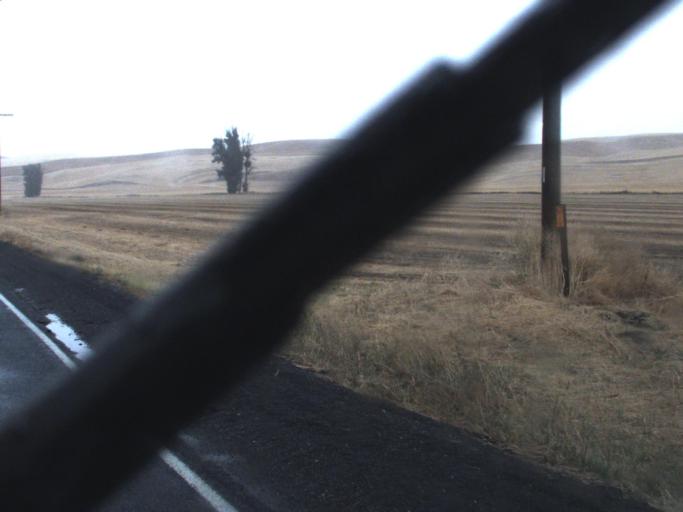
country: US
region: Washington
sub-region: Whitman County
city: Colfax
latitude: 47.0283
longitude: -117.4965
